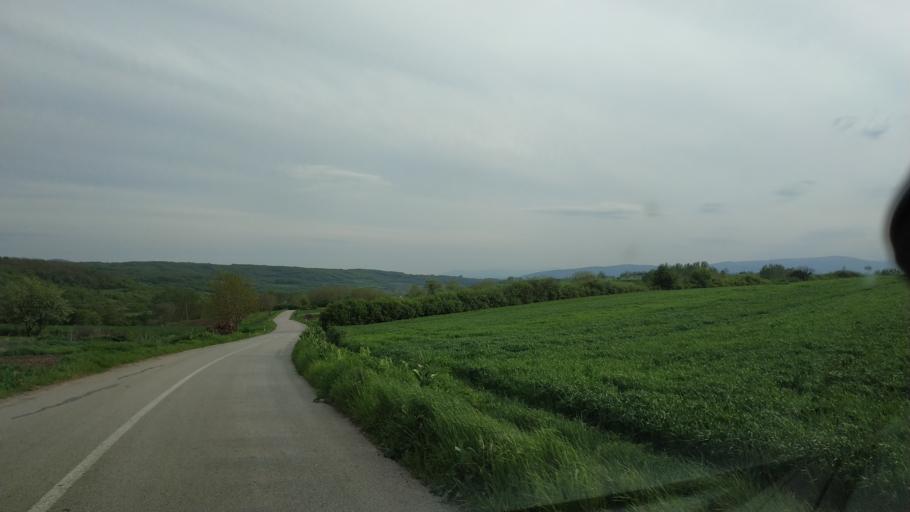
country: RS
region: Central Serbia
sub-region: Zajecarski Okrug
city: Soko Banja
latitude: 43.5236
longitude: 21.8483
